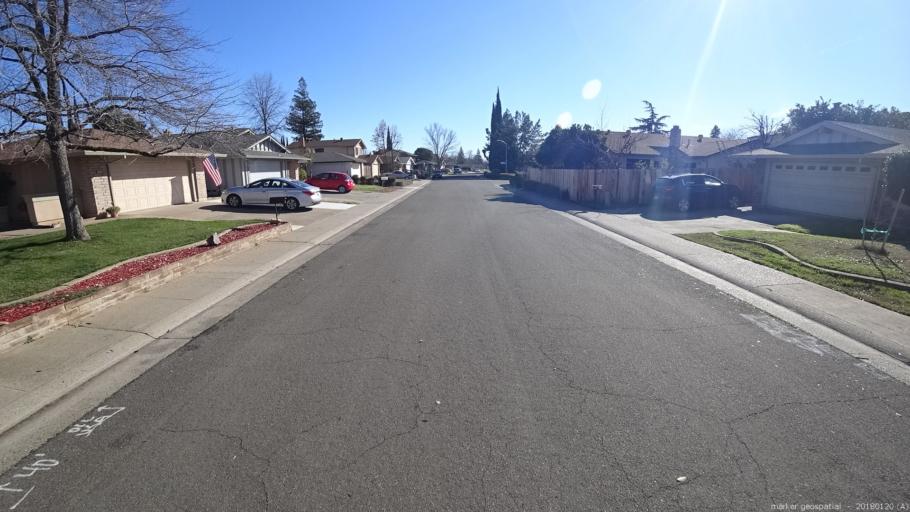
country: US
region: California
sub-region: Sacramento County
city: Rancho Cordova
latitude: 38.5690
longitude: -121.3257
